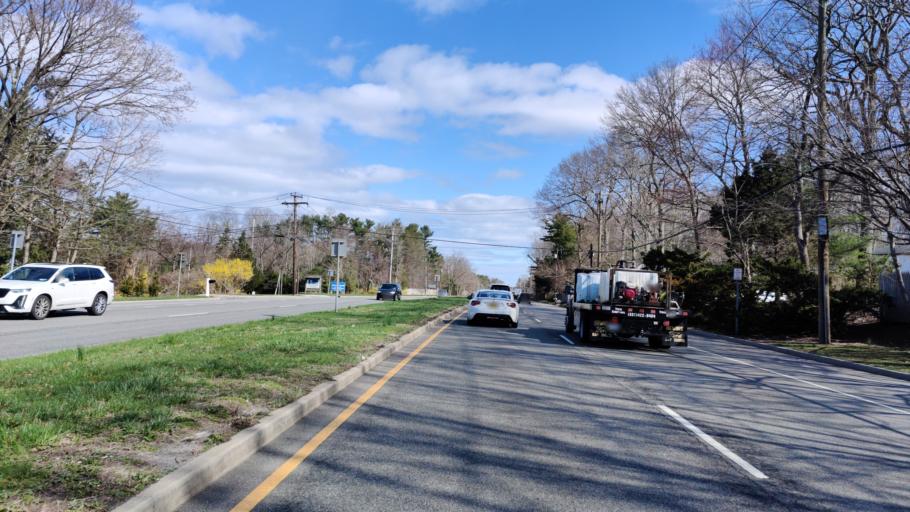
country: US
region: New York
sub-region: Suffolk County
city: Dix Hills
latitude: 40.8001
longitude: -73.3425
